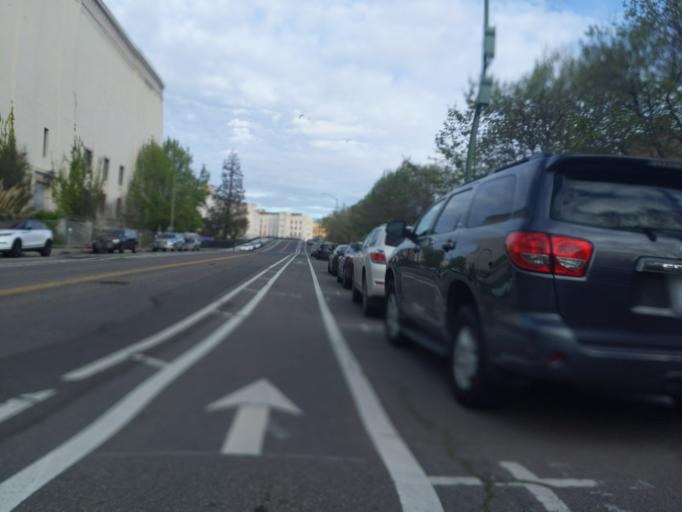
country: US
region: California
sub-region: Alameda County
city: Oakland
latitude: 37.7972
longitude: -122.2620
